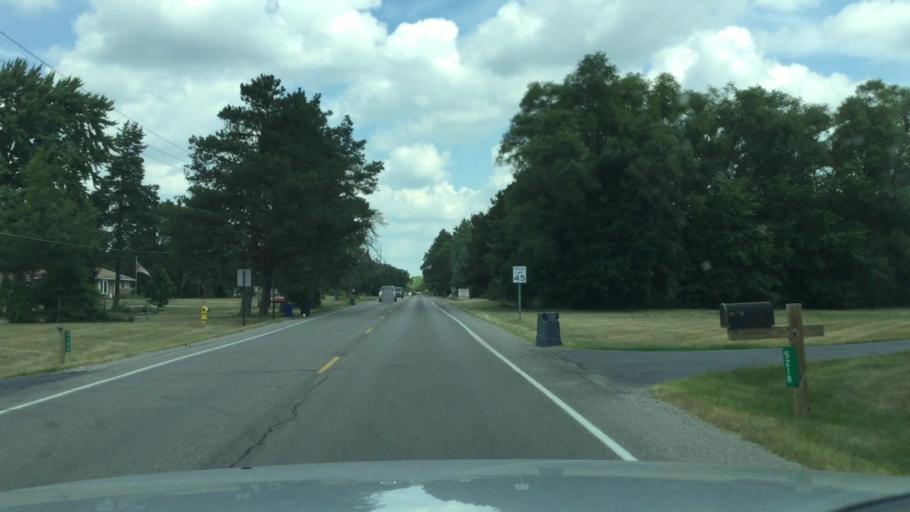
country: US
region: Michigan
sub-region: Genesee County
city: Flushing
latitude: 43.0790
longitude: -83.8702
